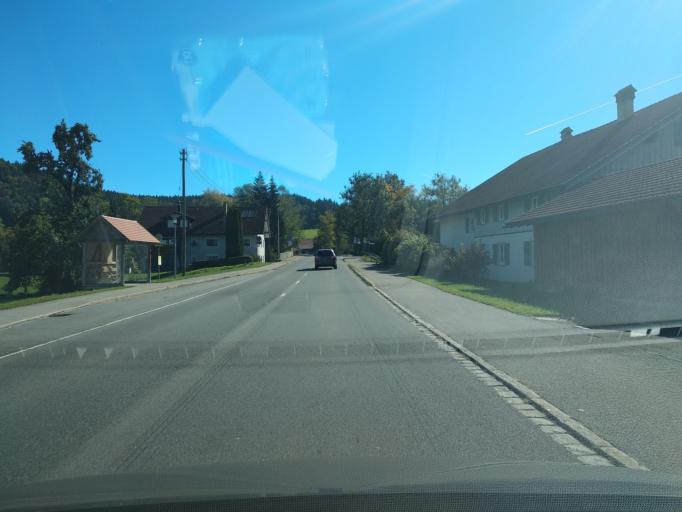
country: DE
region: Bavaria
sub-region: Swabia
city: Maierhofen
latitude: 47.6806
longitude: 10.0831
